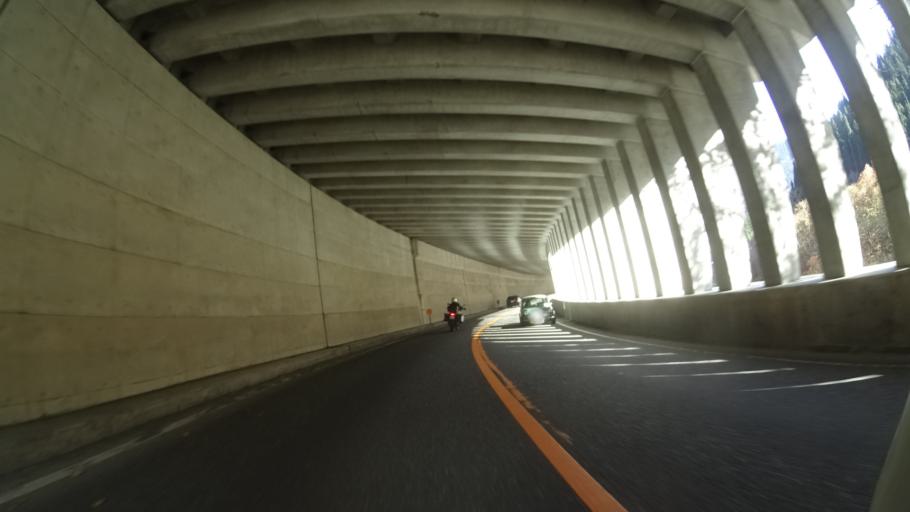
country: JP
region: Fukui
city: Ono
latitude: 35.9280
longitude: 136.6362
